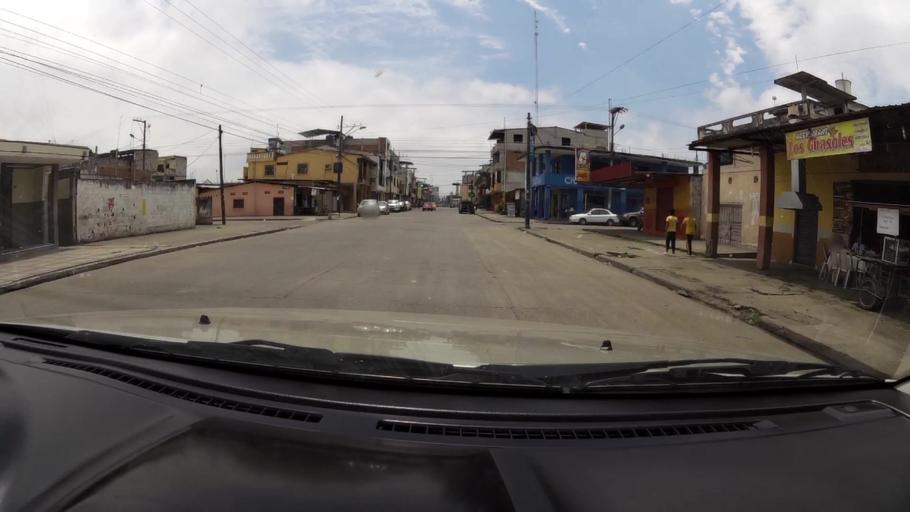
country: EC
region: El Oro
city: Pasaje
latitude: -3.2431
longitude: -79.8280
